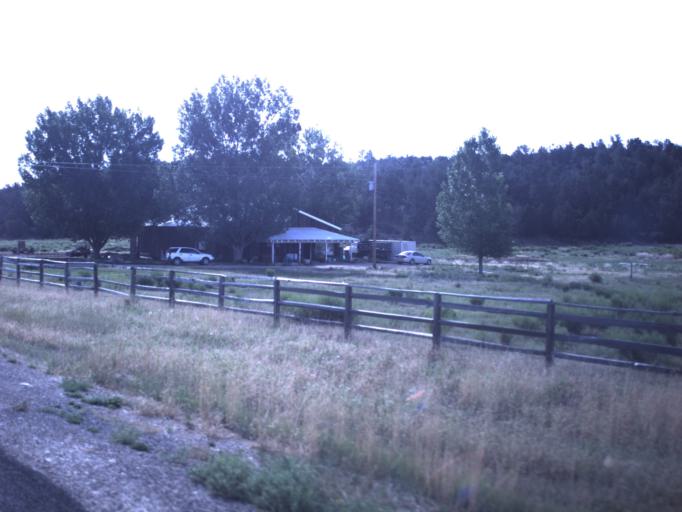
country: US
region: Utah
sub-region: Washington County
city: Hildale
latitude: 37.2391
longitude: -112.8325
